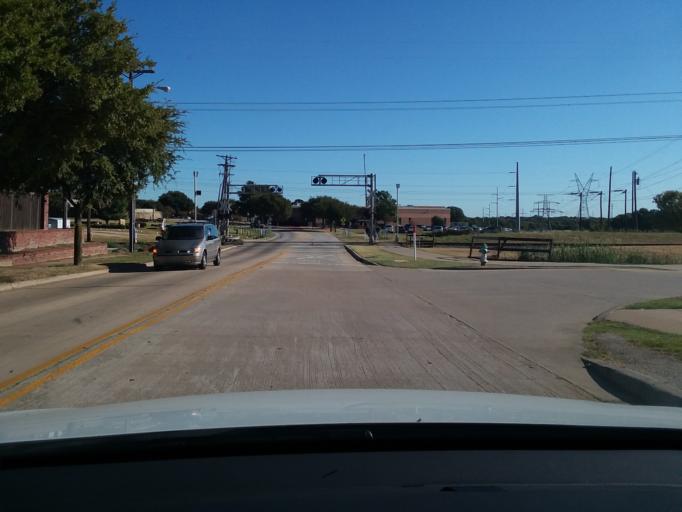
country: US
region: Texas
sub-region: Denton County
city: Highland Village
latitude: 33.0791
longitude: -97.0672
